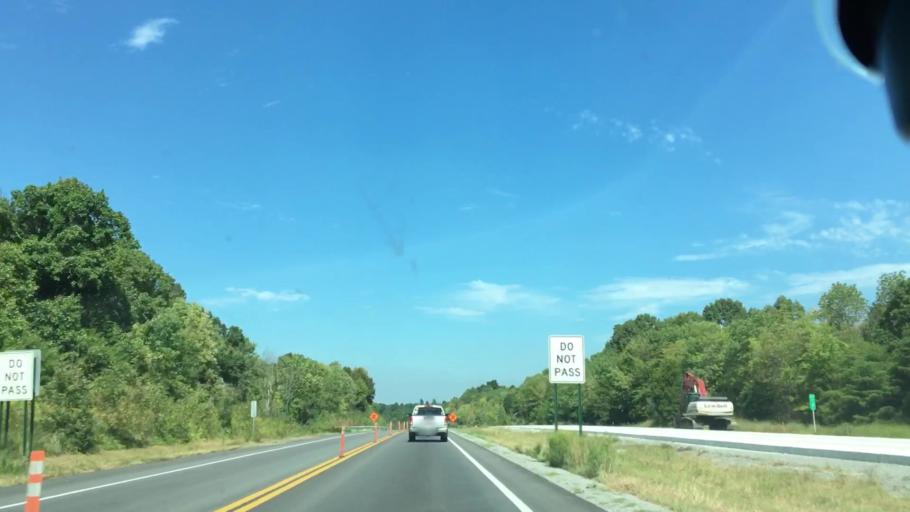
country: US
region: Kentucky
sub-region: Christian County
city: Hopkinsville
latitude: 36.9700
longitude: -87.4655
